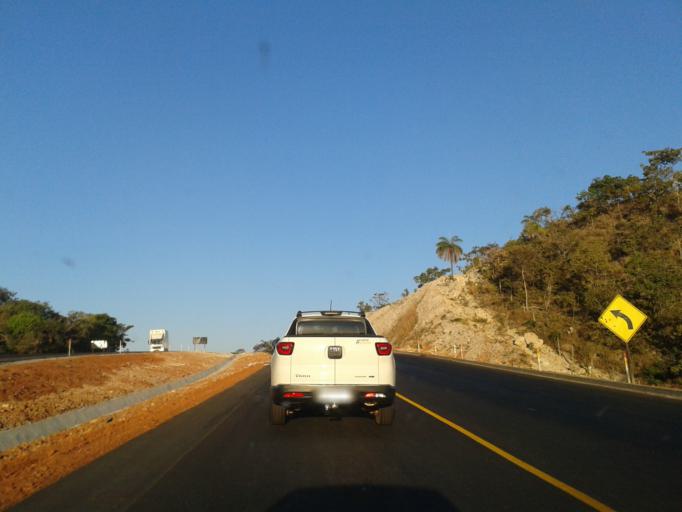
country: BR
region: Goias
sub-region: Goias
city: Goias
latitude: -16.0023
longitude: -50.0670
